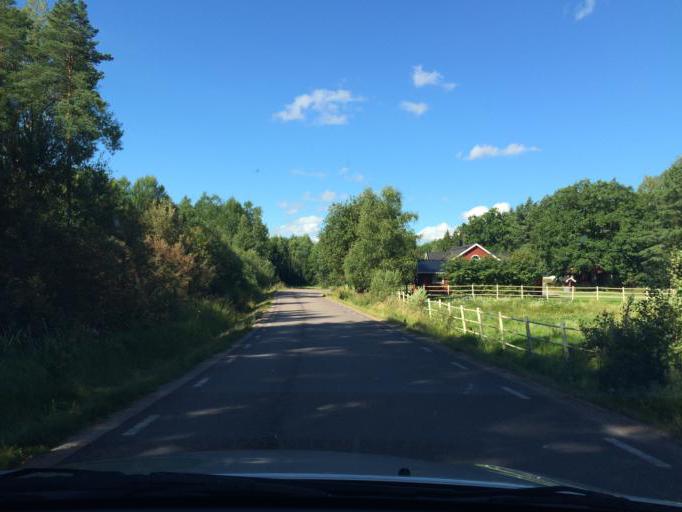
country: SE
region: Soedermanland
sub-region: Eskilstuna Kommun
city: Kvicksund
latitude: 59.4952
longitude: 16.3151
